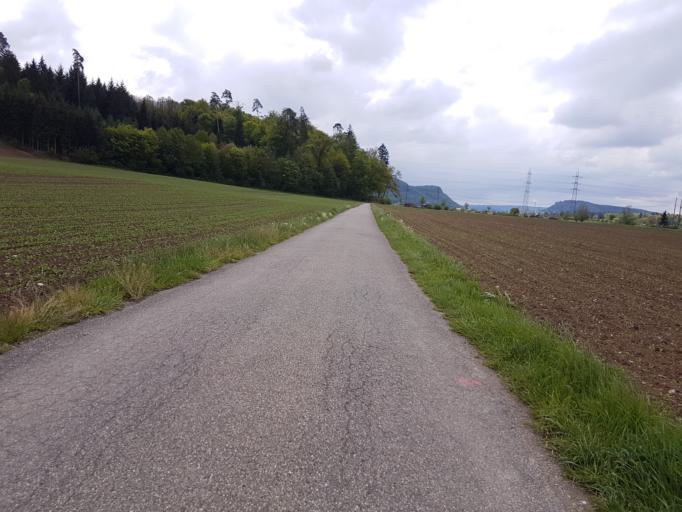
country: CH
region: Aargau
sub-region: Bezirk Baden
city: Wurenlingen
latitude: 47.5517
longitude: 8.2537
